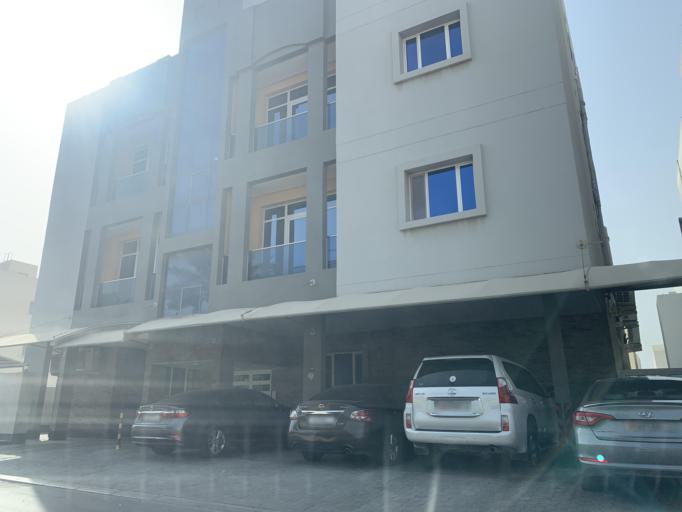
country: BH
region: Northern
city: Madinat `Isa
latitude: 26.1895
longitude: 50.5624
